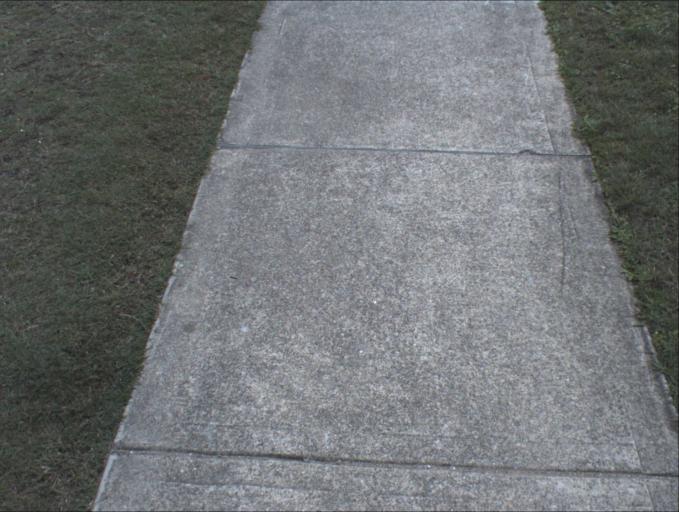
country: AU
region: Queensland
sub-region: Logan
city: Waterford West
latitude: -27.6861
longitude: 153.1512
